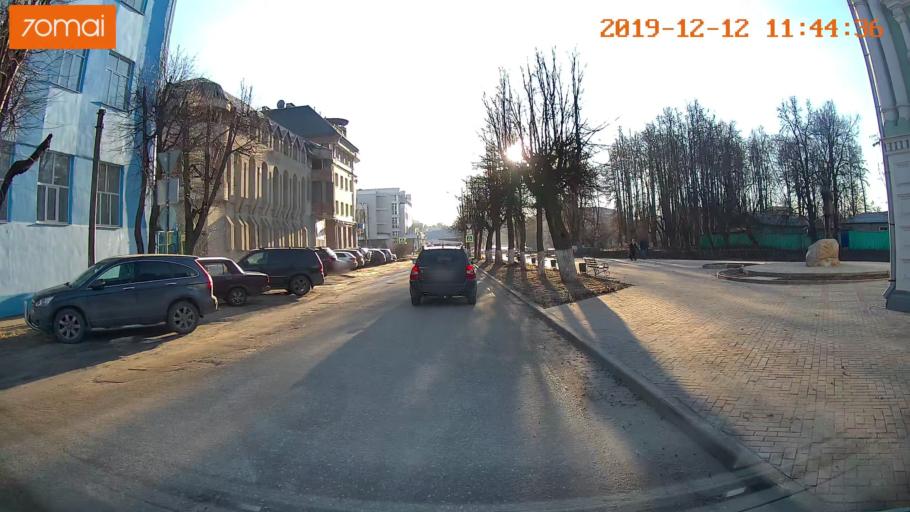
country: RU
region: Ivanovo
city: Shuya
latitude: 56.8541
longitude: 41.3747
